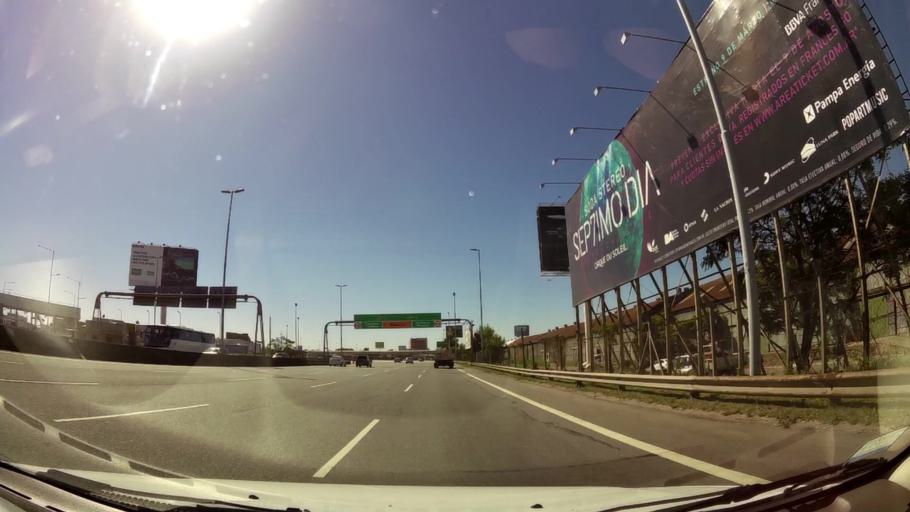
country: AR
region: Buenos Aires F.D.
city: Retiro
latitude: -34.5737
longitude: -58.3971
